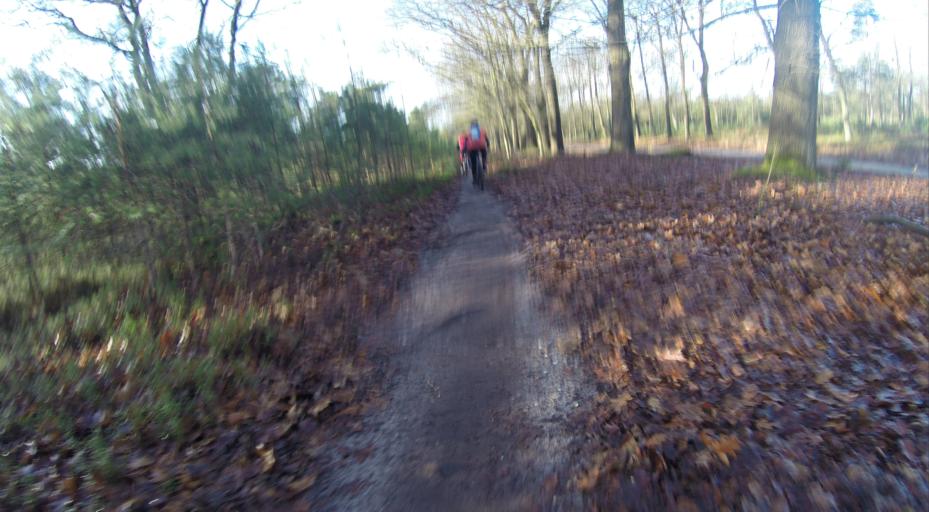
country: NL
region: Overijssel
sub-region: Gemeente Hof van Twente
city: Markelo
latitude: 52.3230
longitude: 6.4007
